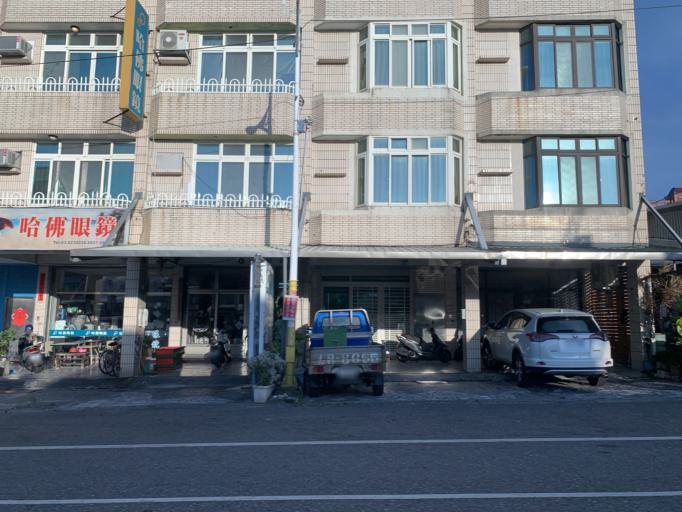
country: TW
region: Taiwan
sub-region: Hualien
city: Hualian
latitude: 23.9967
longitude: 121.6304
